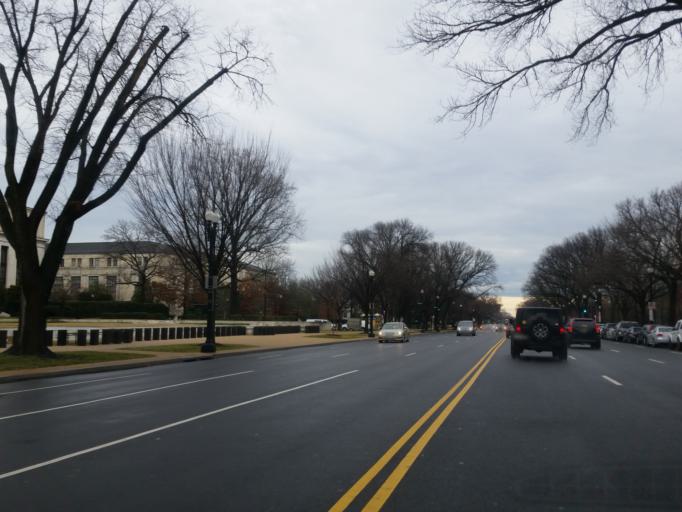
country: US
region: Washington, D.C.
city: Washington, D.C.
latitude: 38.8921
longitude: -77.0464
